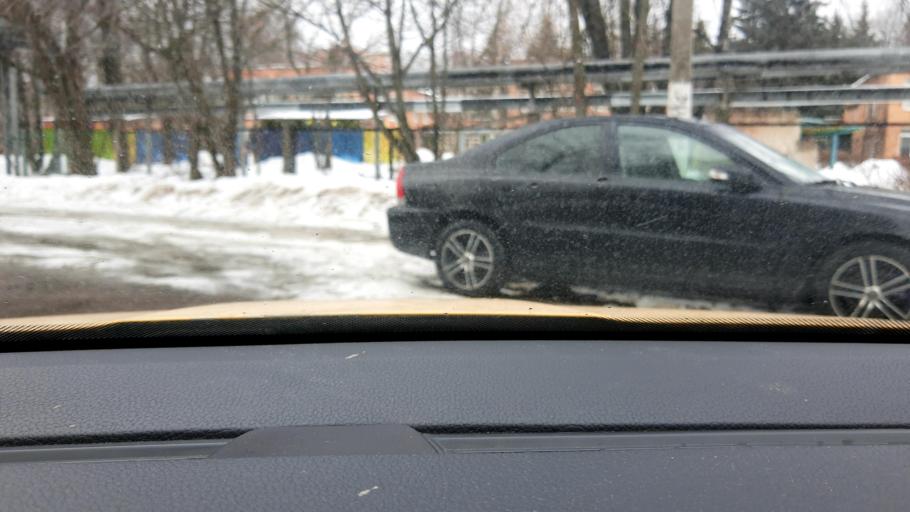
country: RU
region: Moskovskaya
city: Odintsovo
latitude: 55.6820
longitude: 37.2617
